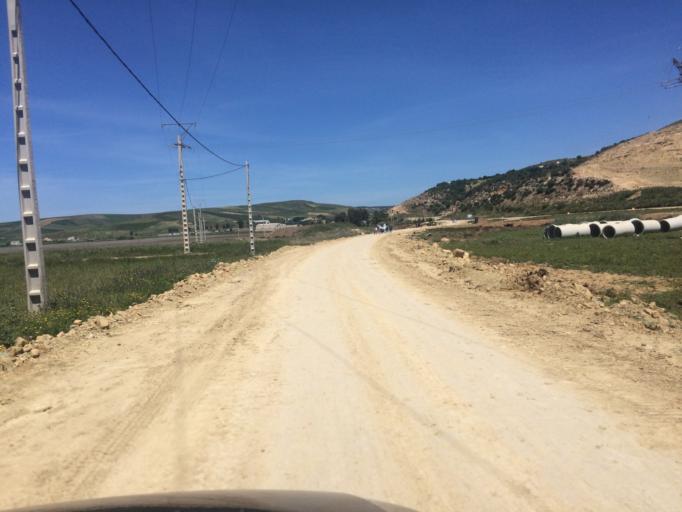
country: MA
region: Tanger-Tetouan
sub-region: Larache
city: Larache
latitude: 35.1929
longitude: -6.0830
